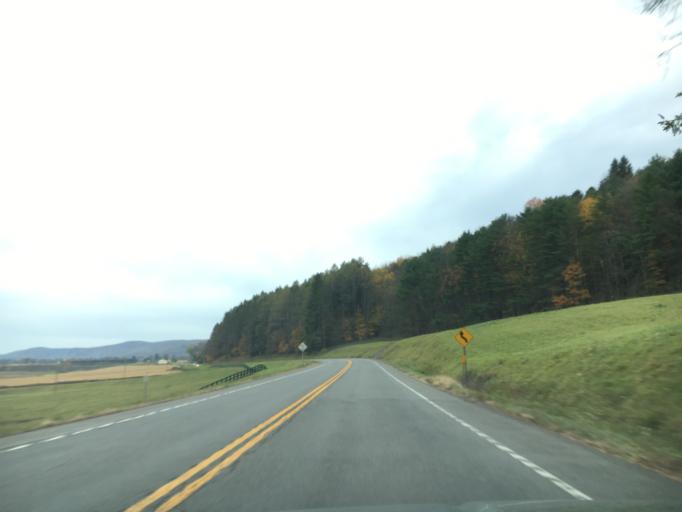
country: US
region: New York
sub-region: Otsego County
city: Cooperstown
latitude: 42.6850
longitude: -74.9424
